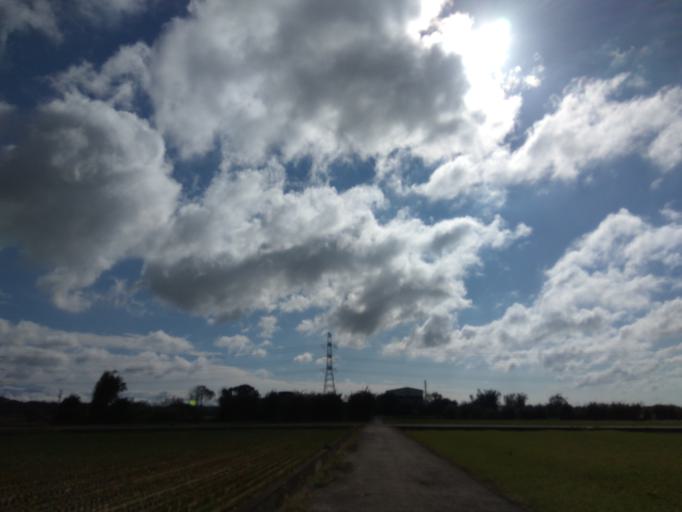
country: TW
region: Taiwan
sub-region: Hsinchu
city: Zhubei
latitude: 24.9709
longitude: 121.0832
